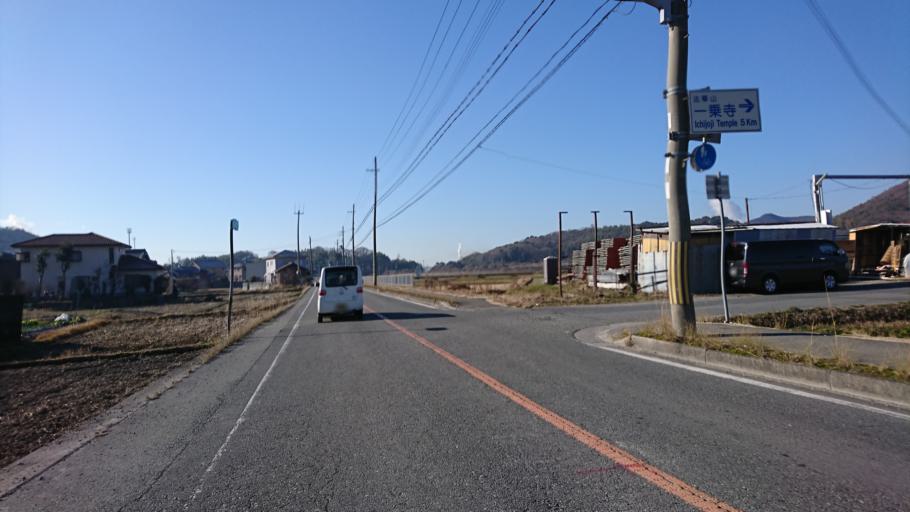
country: JP
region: Hyogo
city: Kakogawacho-honmachi
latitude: 34.8289
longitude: 134.8375
